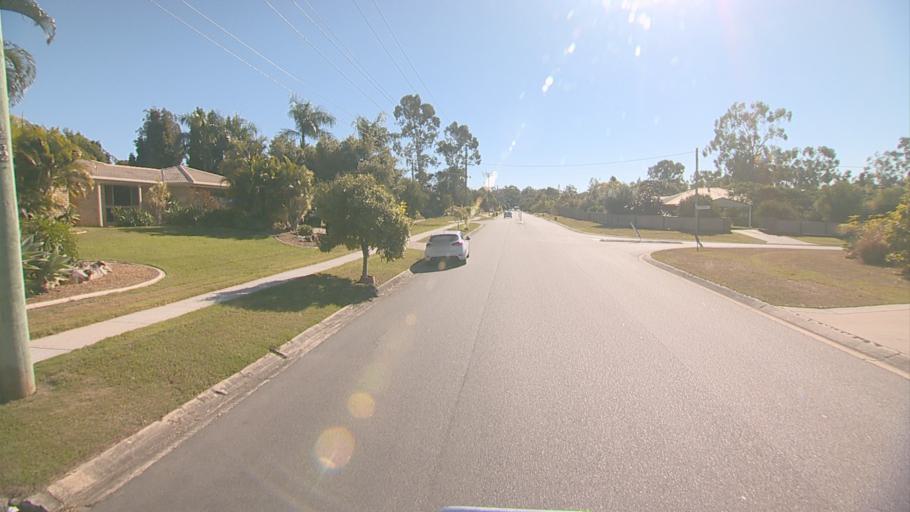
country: AU
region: Queensland
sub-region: Logan
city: Logan Reserve
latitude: -27.6825
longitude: 153.0646
